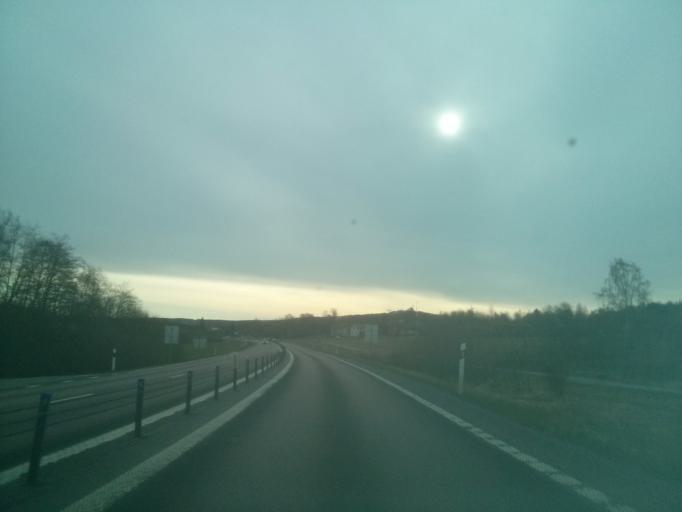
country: SE
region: Vaesternorrland
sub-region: Haernoesands Kommun
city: Haernoesand
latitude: 62.6104
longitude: 17.8748
